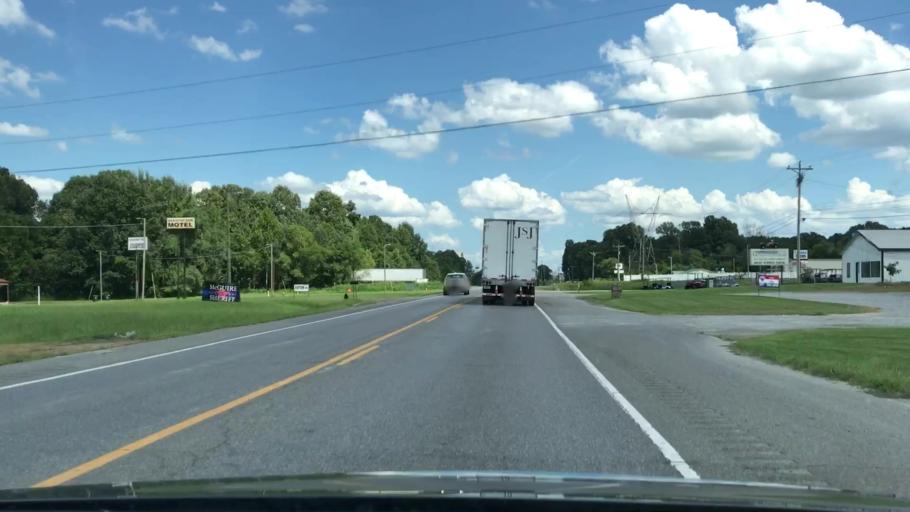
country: US
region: Kentucky
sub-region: Marshall County
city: Calvert City
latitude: 37.0035
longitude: -88.3395
